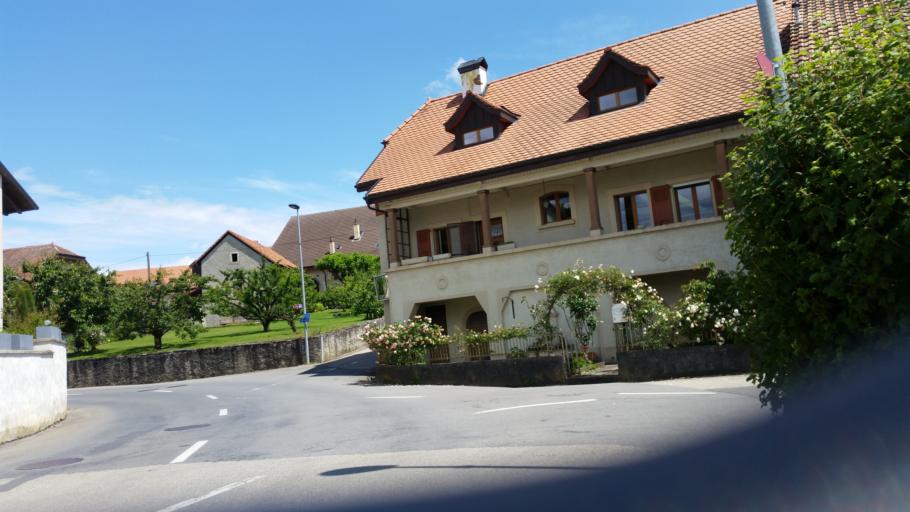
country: CH
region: Vaud
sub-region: Jura-Nord vaudois District
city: Chavornay
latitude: 46.7219
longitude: 6.5982
